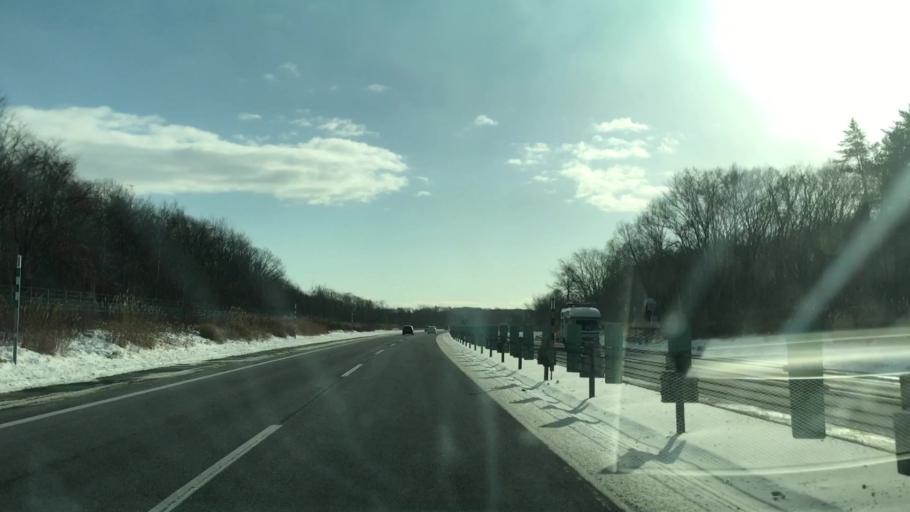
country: JP
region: Hokkaido
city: Chitose
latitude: 42.8386
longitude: 141.6027
